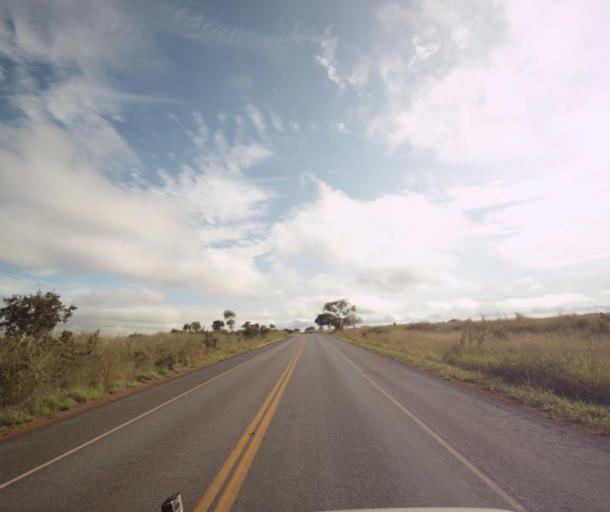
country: BR
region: Goias
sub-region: Padre Bernardo
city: Padre Bernardo
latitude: -15.4648
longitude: -48.6137
